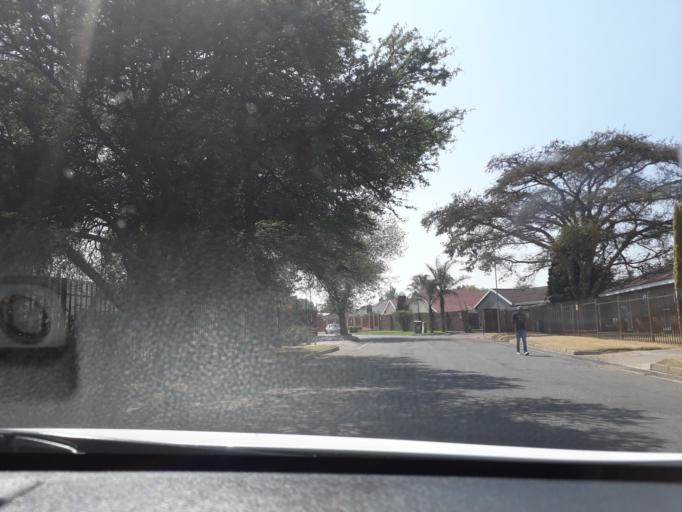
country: ZA
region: Gauteng
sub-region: City of Johannesburg Metropolitan Municipality
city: Modderfontein
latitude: -26.0909
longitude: 28.2281
